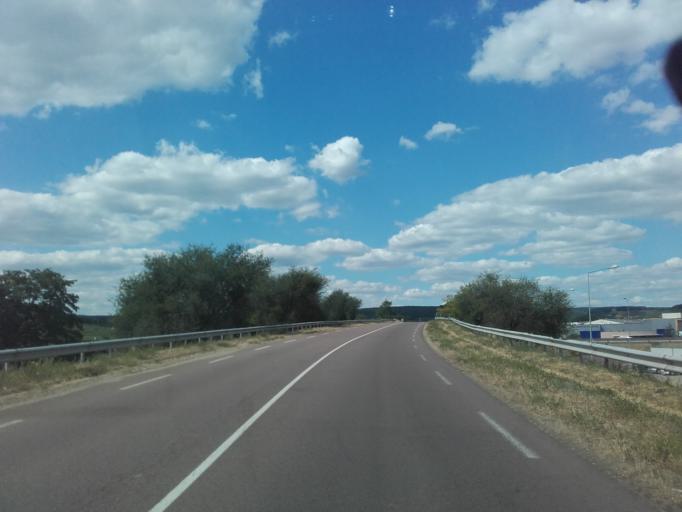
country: FR
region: Bourgogne
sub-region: Departement de la Cote-d'Or
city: Beaune
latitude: 47.0430
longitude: 4.8396
